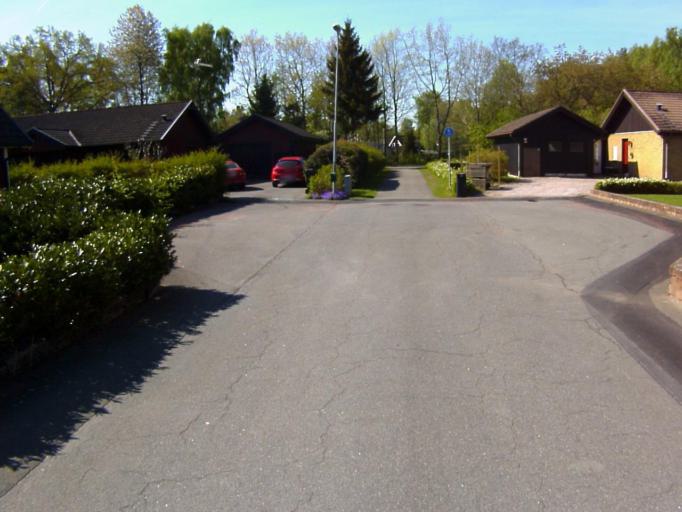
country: SE
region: Skane
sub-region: Kristianstads Kommun
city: Onnestad
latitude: 55.9412
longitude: 13.9842
